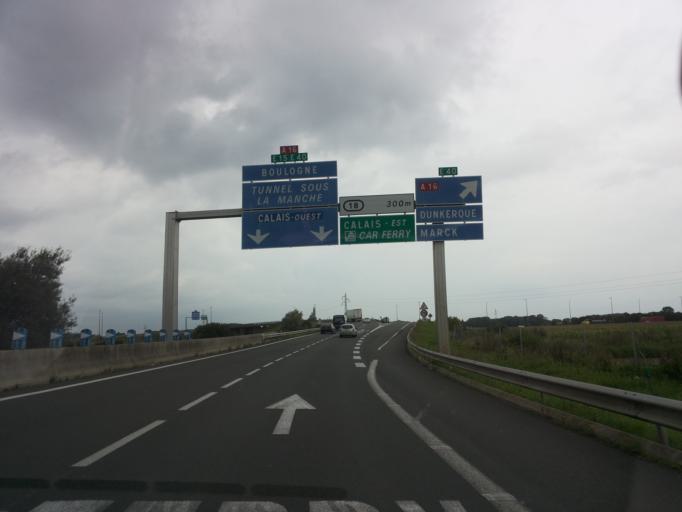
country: FR
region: Nord-Pas-de-Calais
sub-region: Departement du Pas-de-Calais
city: Coulogne
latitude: 50.9334
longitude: 1.9099
